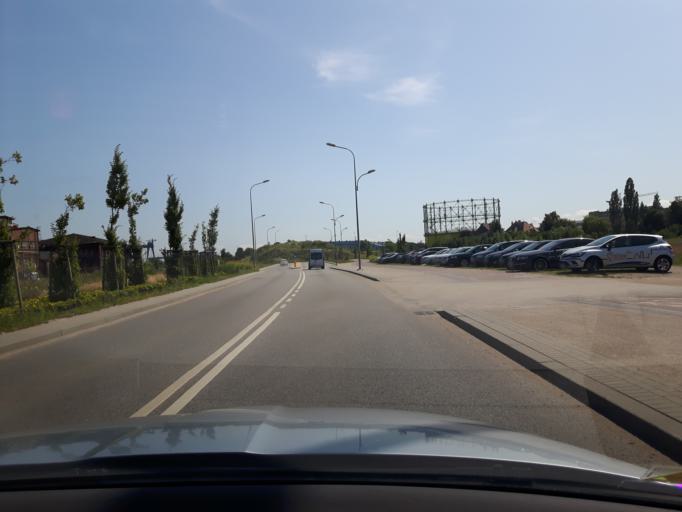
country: PL
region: Pomeranian Voivodeship
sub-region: Gdansk
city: Gdansk
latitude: 54.3611
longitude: 18.6547
